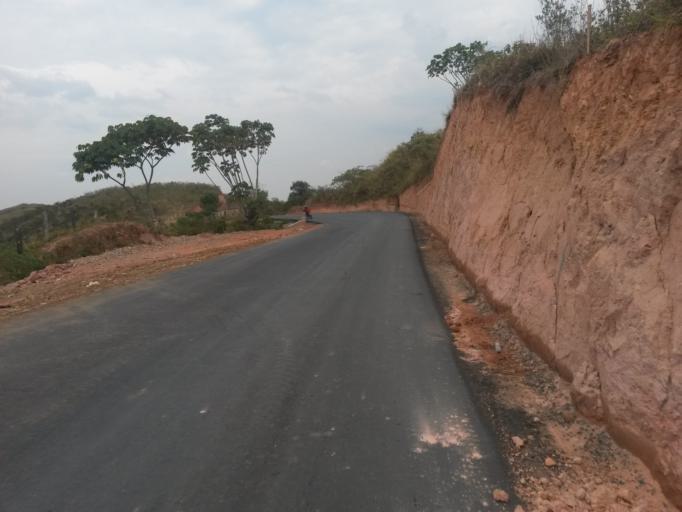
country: CO
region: Cauca
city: Buenos Aires
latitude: 3.0563
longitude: -76.6294
